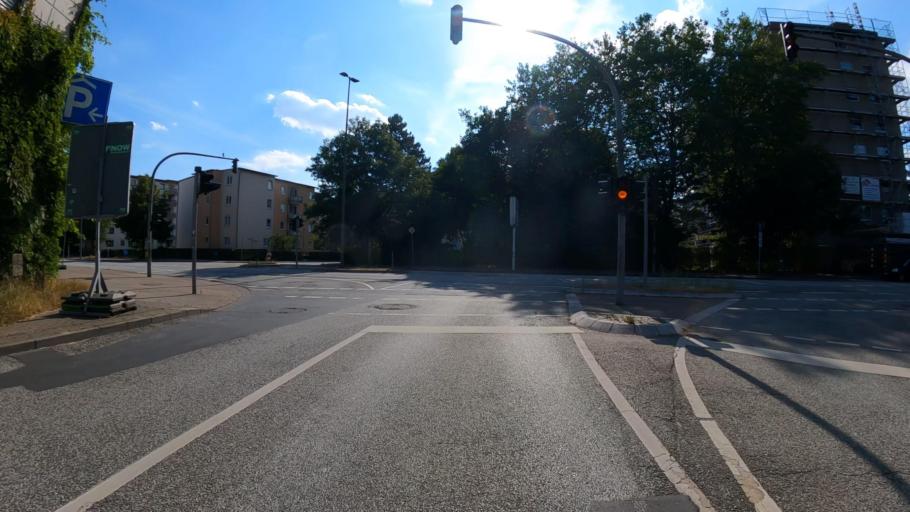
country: DE
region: Schleswig-Holstein
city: Norderstedt
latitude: 53.6856
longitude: 9.9847
